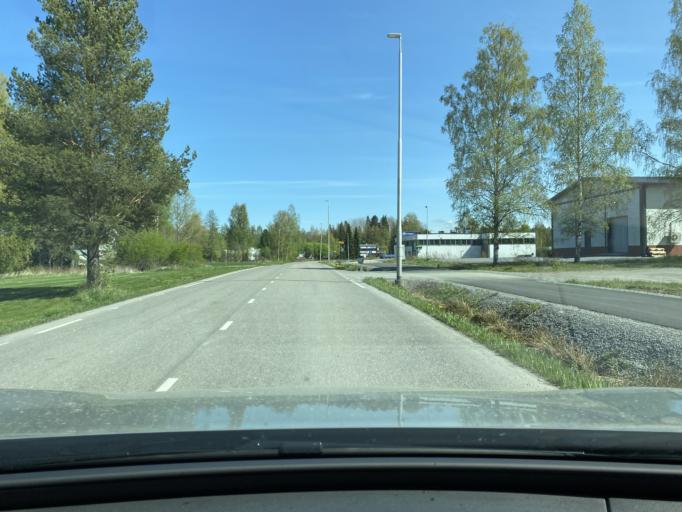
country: FI
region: Pirkanmaa
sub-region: Lounais-Pirkanmaa
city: Vammala
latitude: 61.3300
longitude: 22.9129
